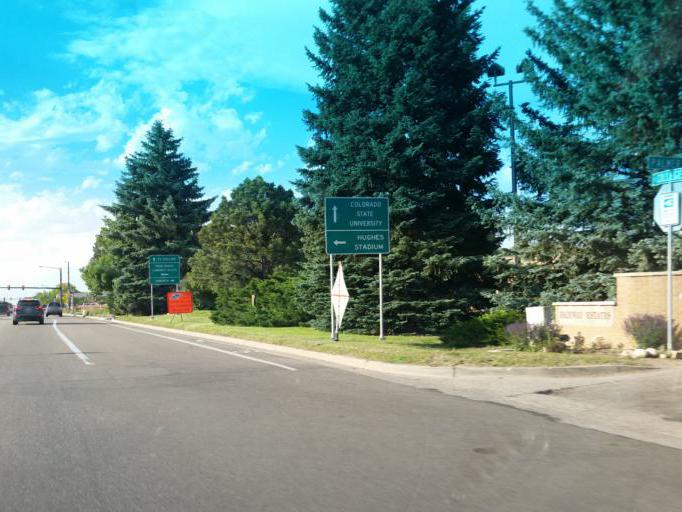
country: US
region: Colorado
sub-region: Larimer County
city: Fort Collins
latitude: 40.5215
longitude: -105.0770
